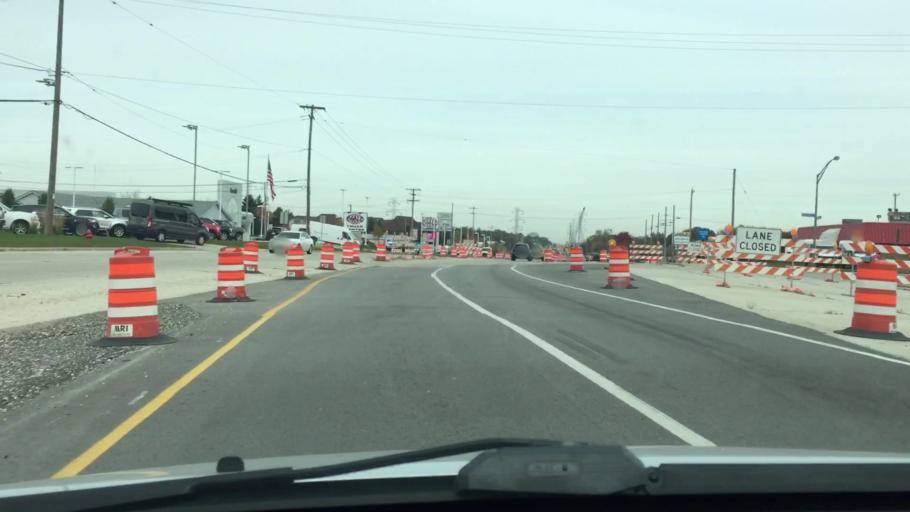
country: US
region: Wisconsin
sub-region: Milwaukee County
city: Hales Corners
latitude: 42.9280
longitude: -88.0485
